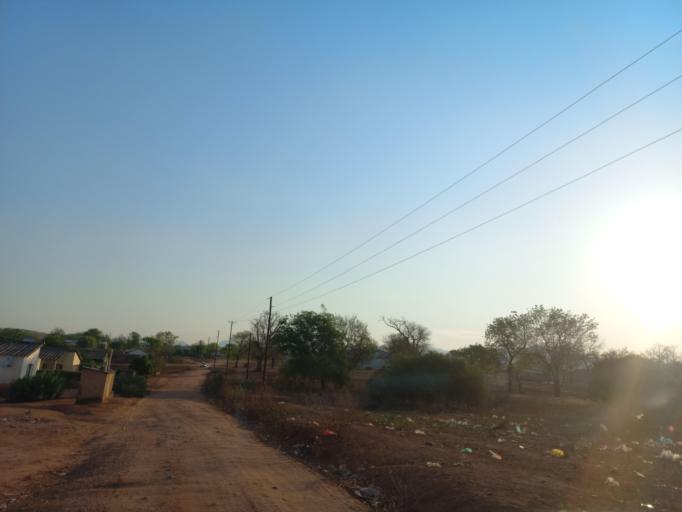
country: ZM
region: Lusaka
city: Luangwa
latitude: -15.6141
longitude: 30.3914
